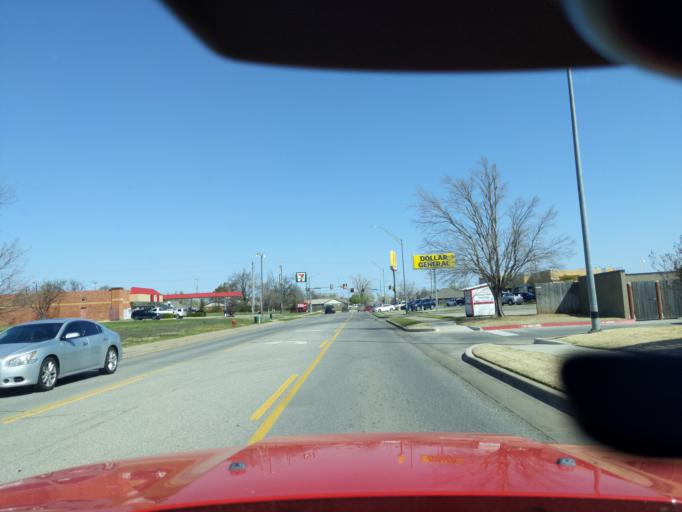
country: US
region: Oklahoma
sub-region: Cleveland County
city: Moore
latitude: 35.3474
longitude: -97.4990
